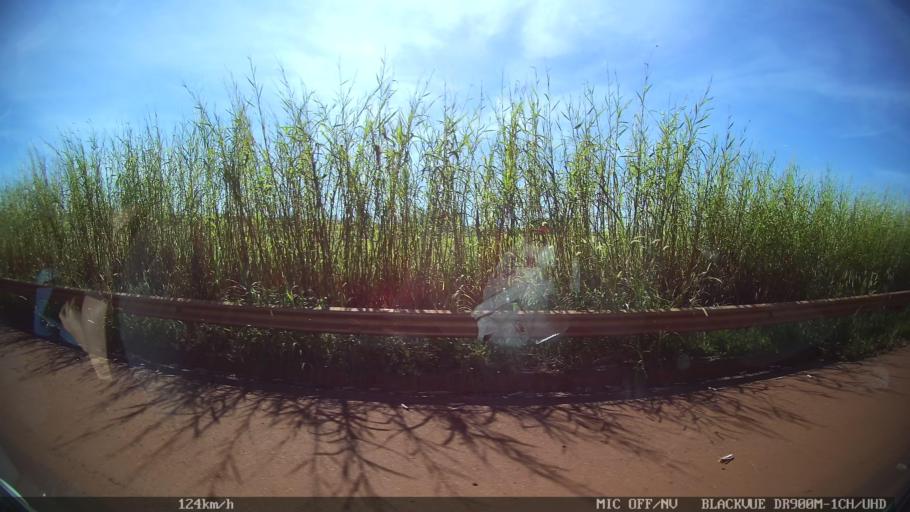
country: BR
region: Sao Paulo
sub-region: Sao Joaquim Da Barra
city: Sao Joaquim da Barra
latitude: -20.5475
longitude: -47.7647
